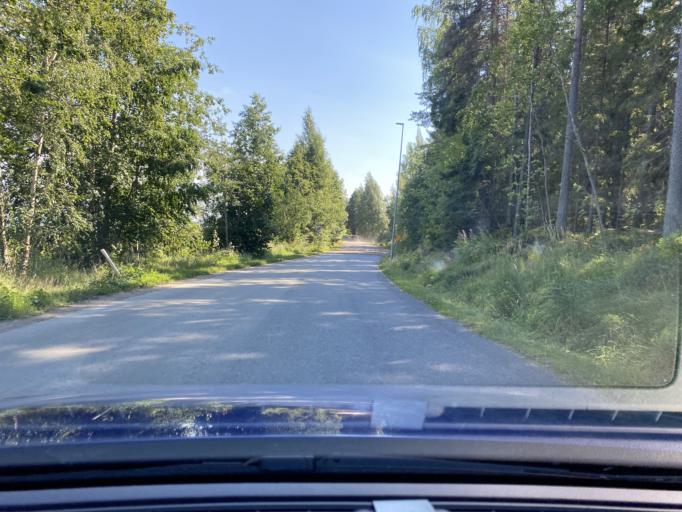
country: FI
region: Central Finland
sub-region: Jyvaeskylae
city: Korpilahti
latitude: 61.8893
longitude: 25.3969
